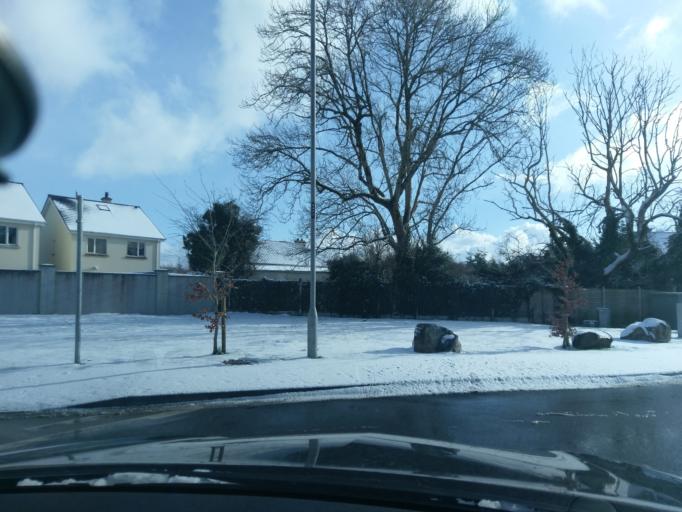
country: IE
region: Connaught
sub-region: County Galway
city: Athenry
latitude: 53.2272
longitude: -8.7377
